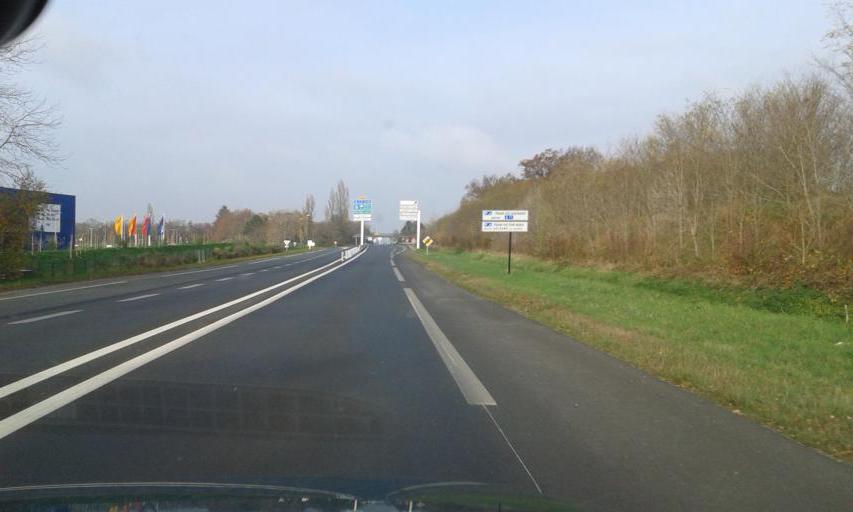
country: FR
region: Centre
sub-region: Departement du Loiret
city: Olivet
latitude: 47.8264
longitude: 1.9215
